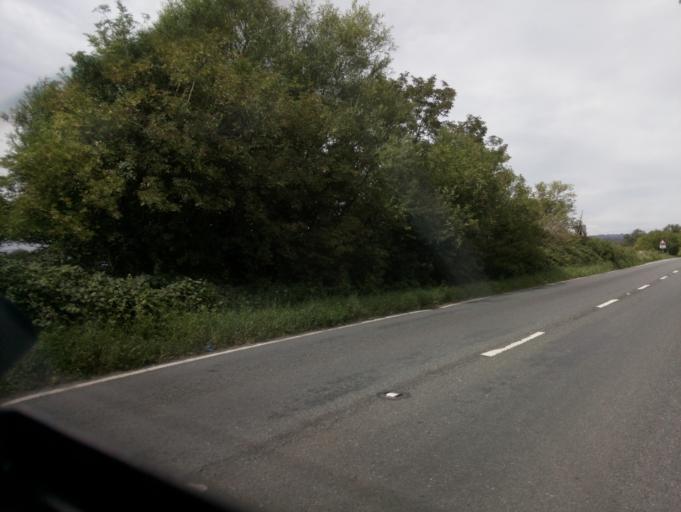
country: GB
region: England
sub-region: Somerset
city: Glastonbury
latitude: 51.1639
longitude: -2.6995
